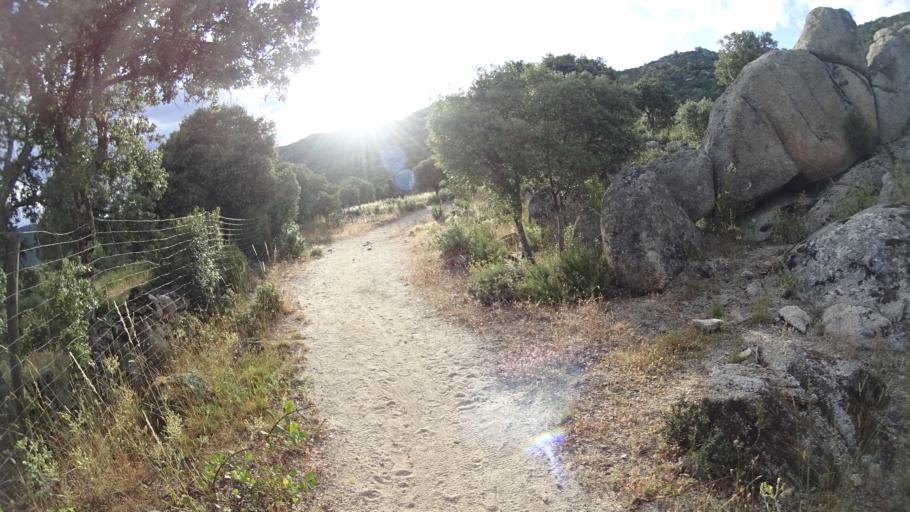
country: ES
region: Madrid
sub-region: Provincia de Madrid
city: Hoyo de Manzanares
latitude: 40.6350
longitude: -3.9047
